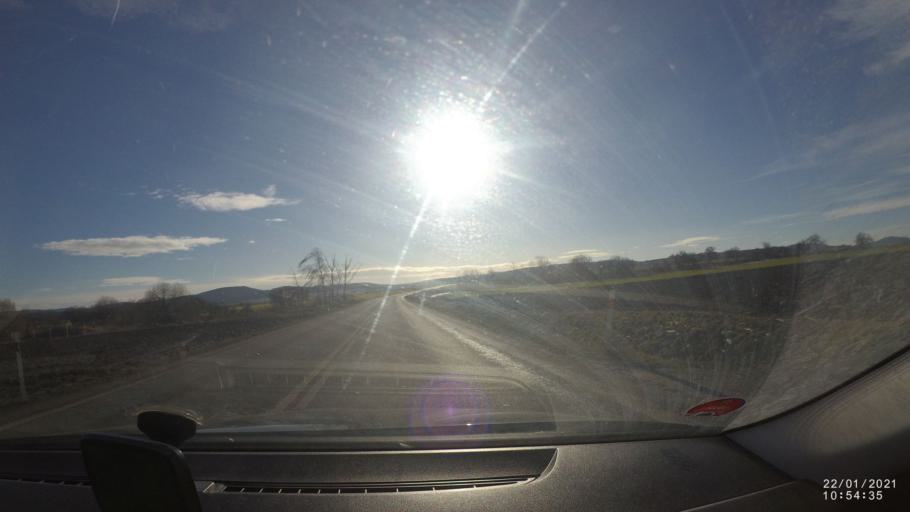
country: CZ
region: Central Bohemia
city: Zebrak
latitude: 49.8568
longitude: 13.9056
